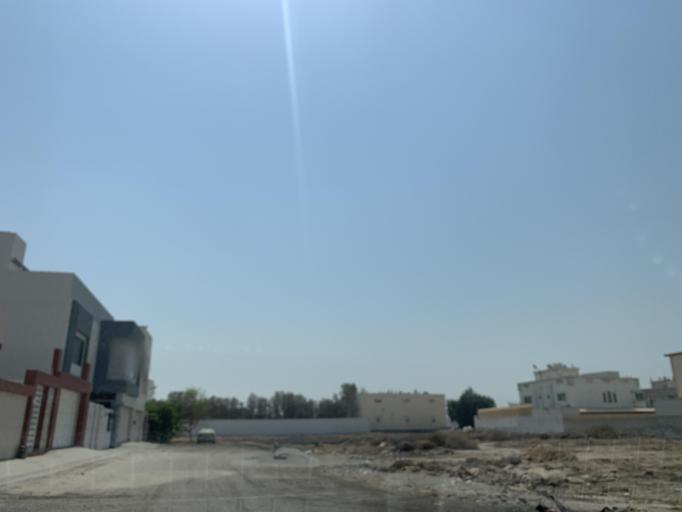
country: BH
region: Manama
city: Jidd Hafs
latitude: 26.2074
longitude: 50.5217
